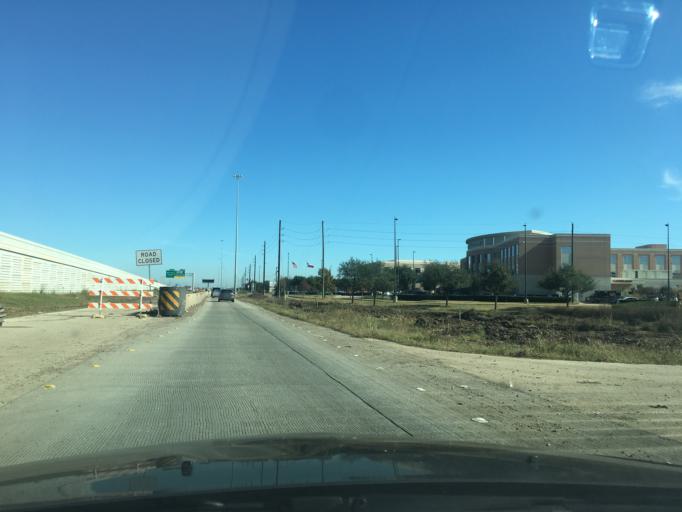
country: US
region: Texas
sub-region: Fort Bend County
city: Greatwood
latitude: 29.5557
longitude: -95.7158
